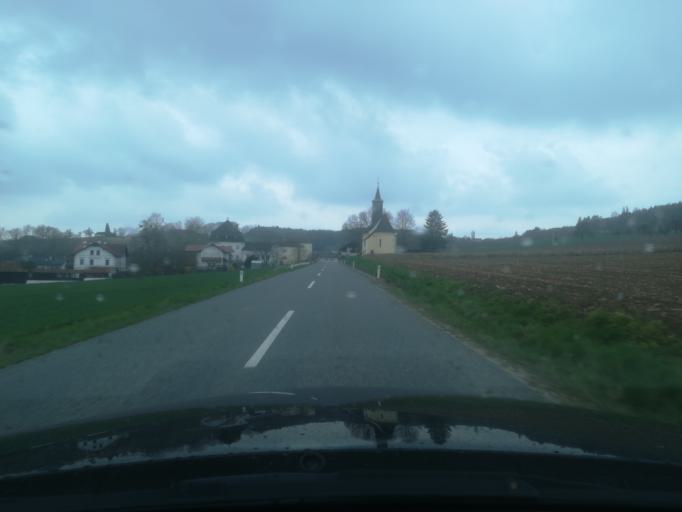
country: AT
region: Upper Austria
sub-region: Wels-Land
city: Holzhausen
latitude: 48.2389
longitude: 14.0660
